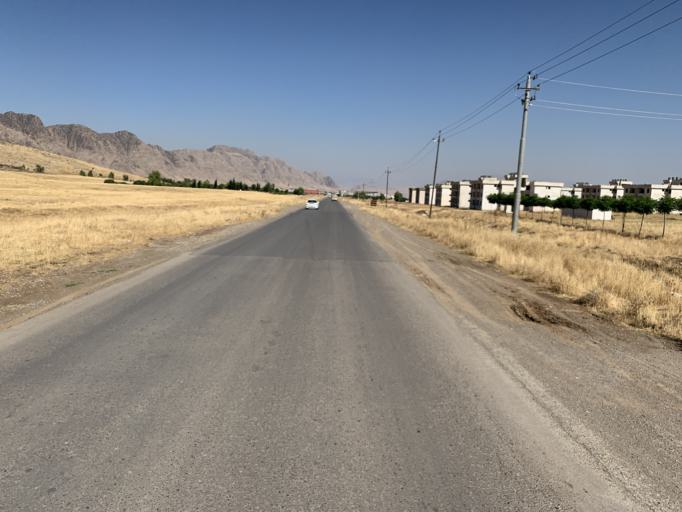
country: IQ
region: As Sulaymaniyah
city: Raniye
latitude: 36.2653
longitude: 44.8425
